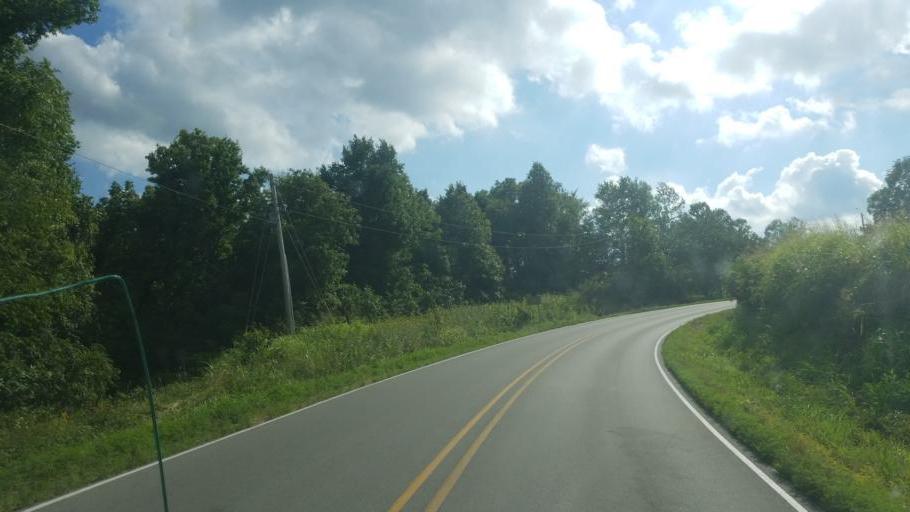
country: US
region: Illinois
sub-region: Union County
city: Cobden
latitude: 37.5477
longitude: -89.2899
